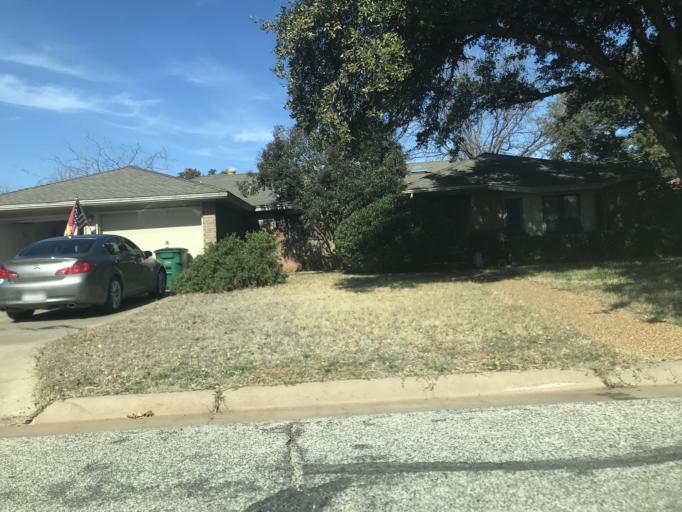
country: US
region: Texas
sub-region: Tom Green County
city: San Angelo
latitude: 31.4278
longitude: -100.4906
